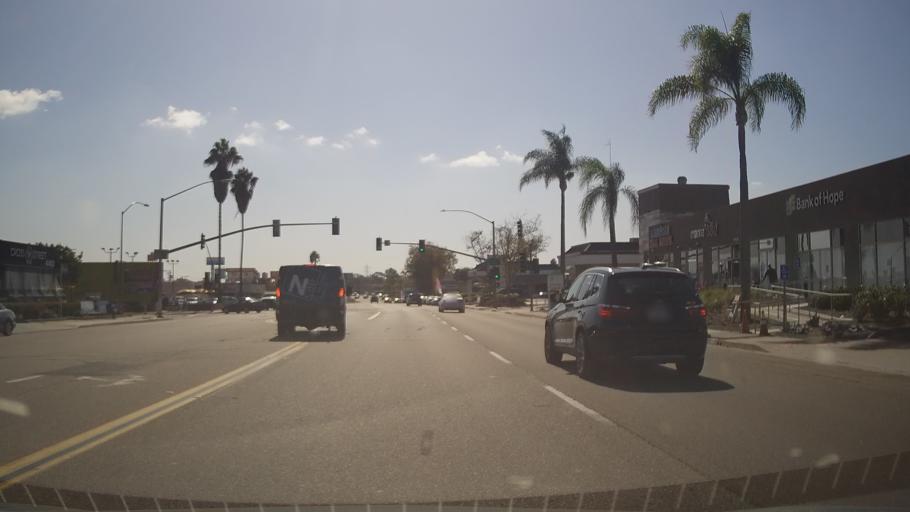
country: US
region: California
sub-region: San Diego County
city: San Diego
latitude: 32.8207
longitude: -117.1551
